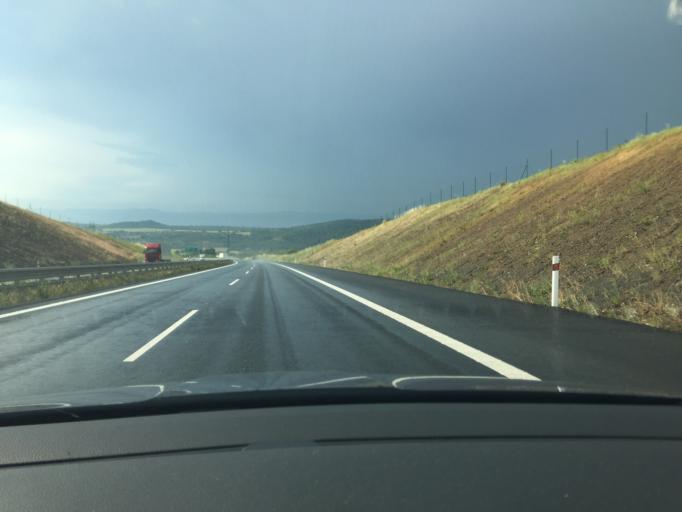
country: CZ
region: Ustecky
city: Rehlovice
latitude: 50.5944
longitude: 13.9733
